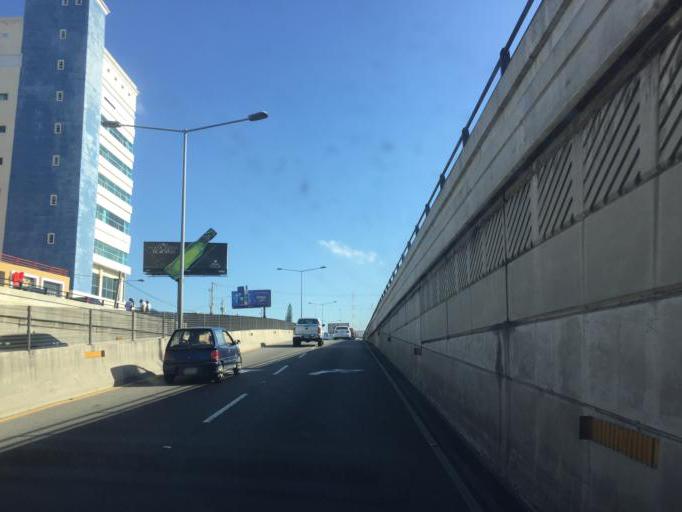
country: DO
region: Nacional
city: Bella Vista
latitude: 18.4551
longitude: -69.9538
